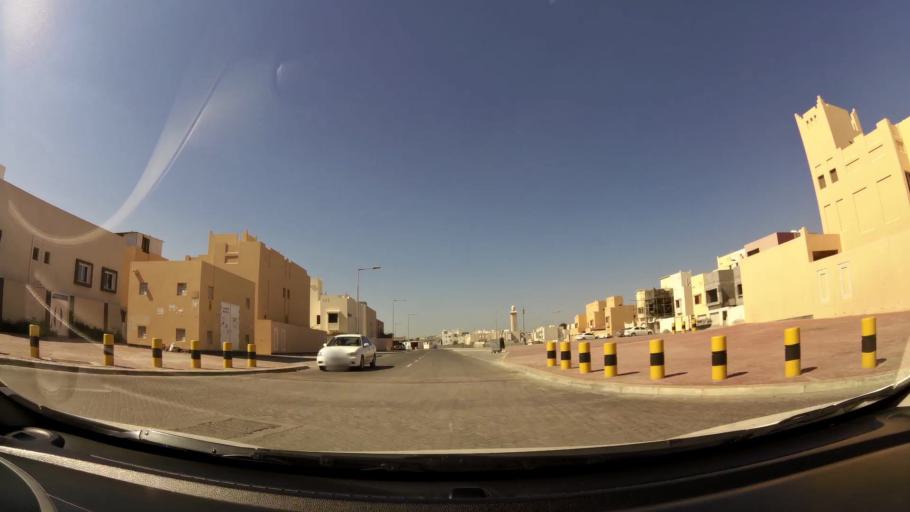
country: BH
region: Muharraq
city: Al Muharraq
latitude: 26.2475
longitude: 50.6319
